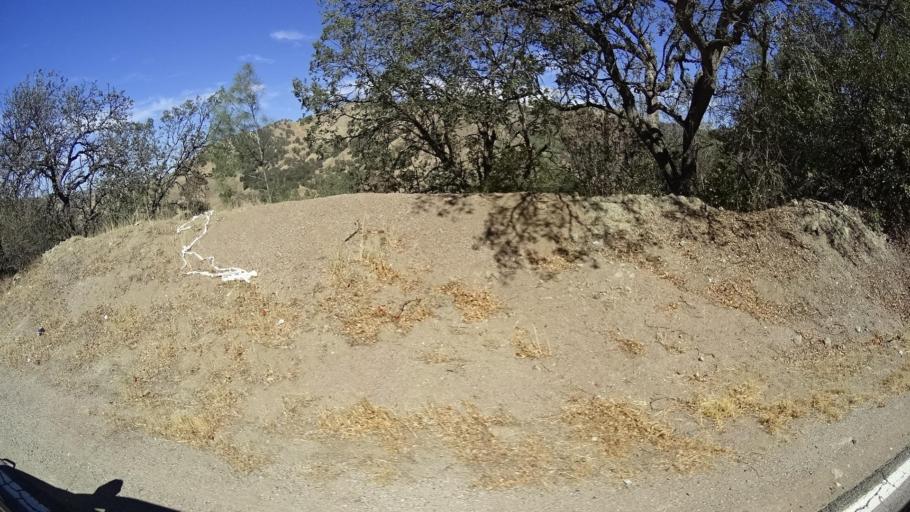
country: US
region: California
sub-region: Fresno County
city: Coalinga
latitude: 36.1957
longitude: -120.7412
